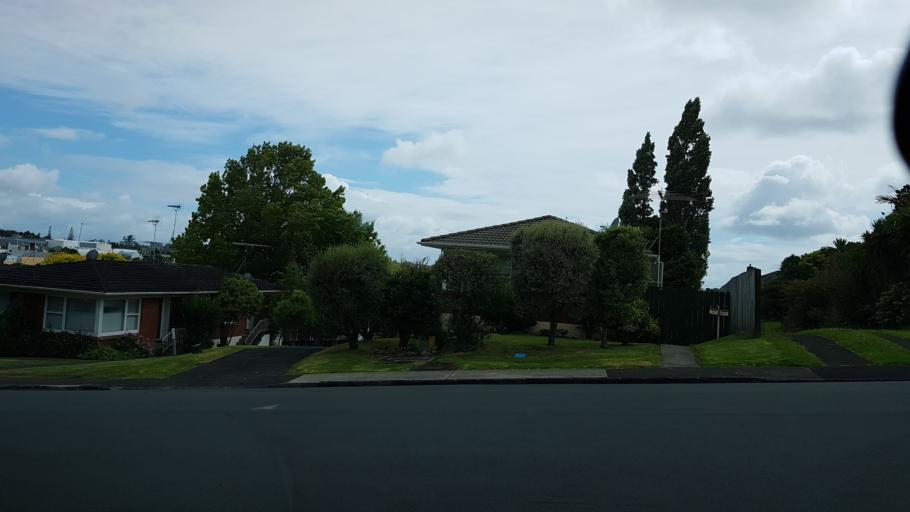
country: NZ
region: Auckland
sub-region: Auckland
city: North Shore
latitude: -36.7872
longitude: 174.7378
